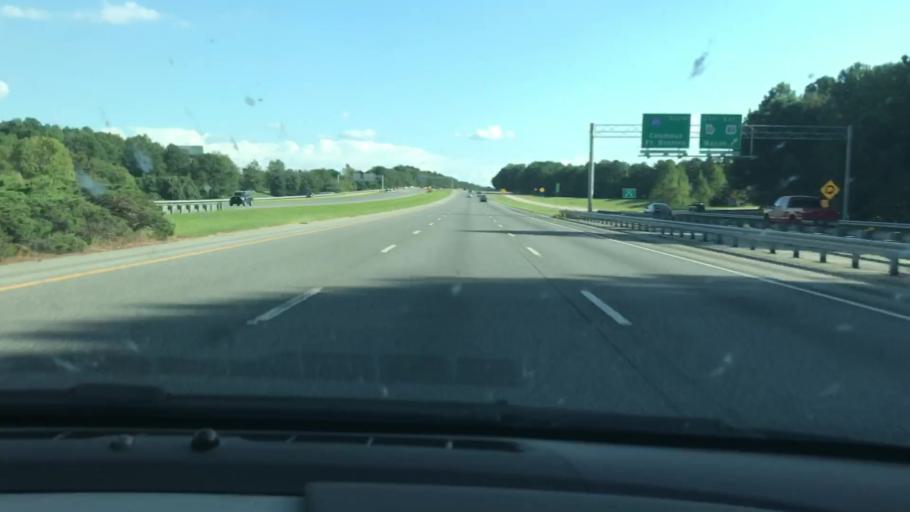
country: US
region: Alabama
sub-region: Russell County
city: Phenix City
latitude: 32.5443
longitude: -84.9610
